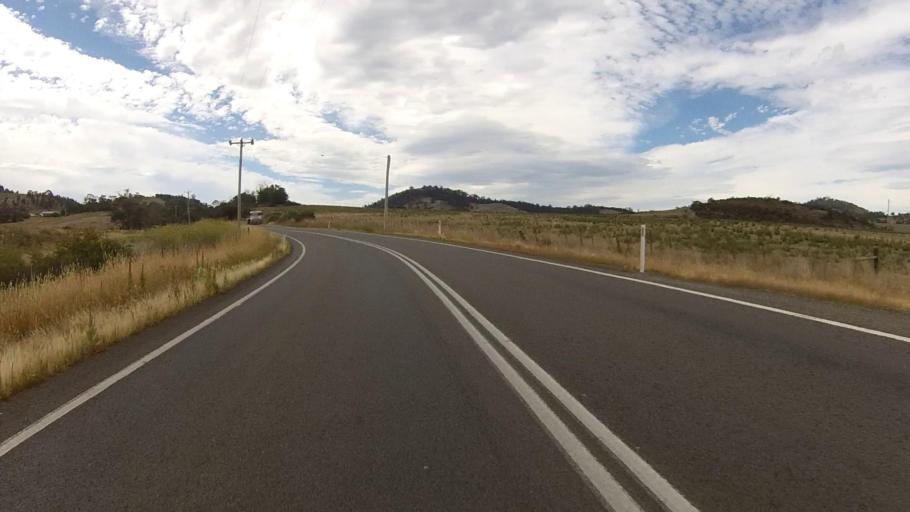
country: AU
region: Tasmania
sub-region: Sorell
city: Sorell
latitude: -42.6942
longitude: 147.4773
